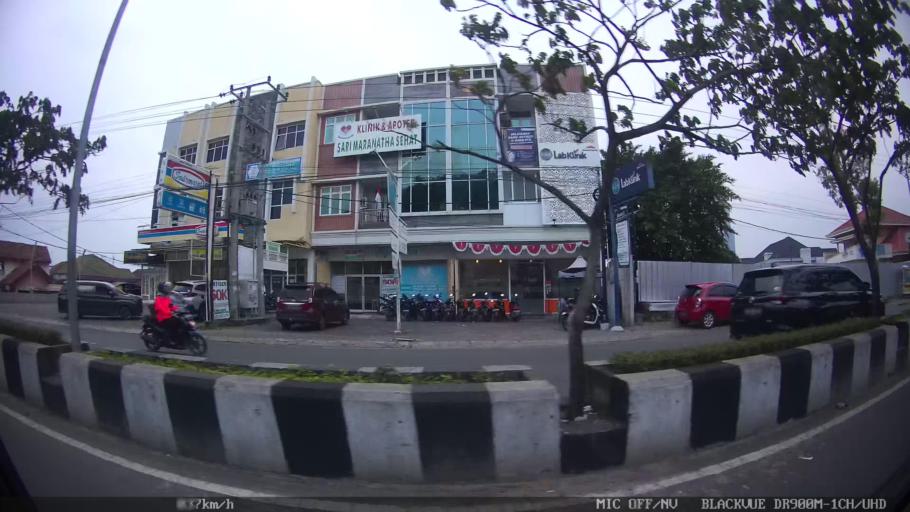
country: ID
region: Lampung
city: Bandarlampung
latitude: -5.4173
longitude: 105.2675
